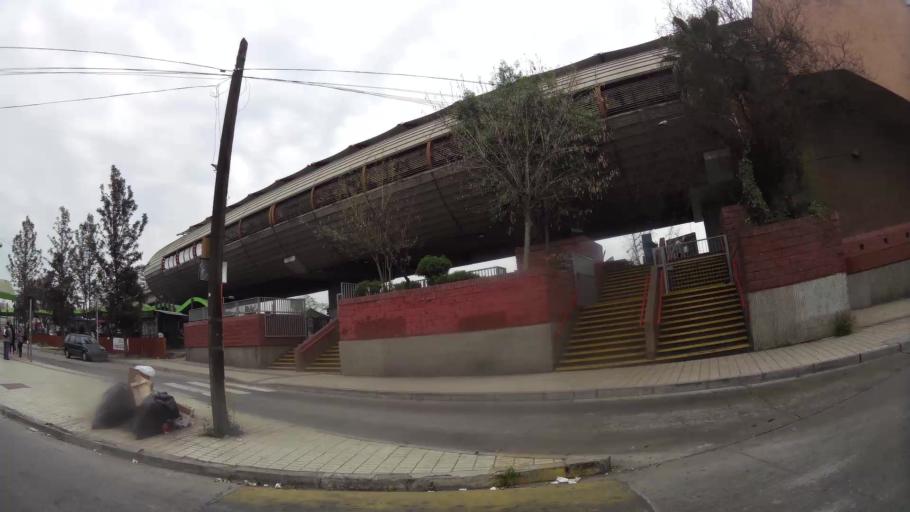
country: CL
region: Santiago Metropolitan
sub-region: Provincia de Santiago
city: Villa Presidente Frei, Nunoa, Santiago, Chile
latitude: -33.5079
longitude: -70.6123
